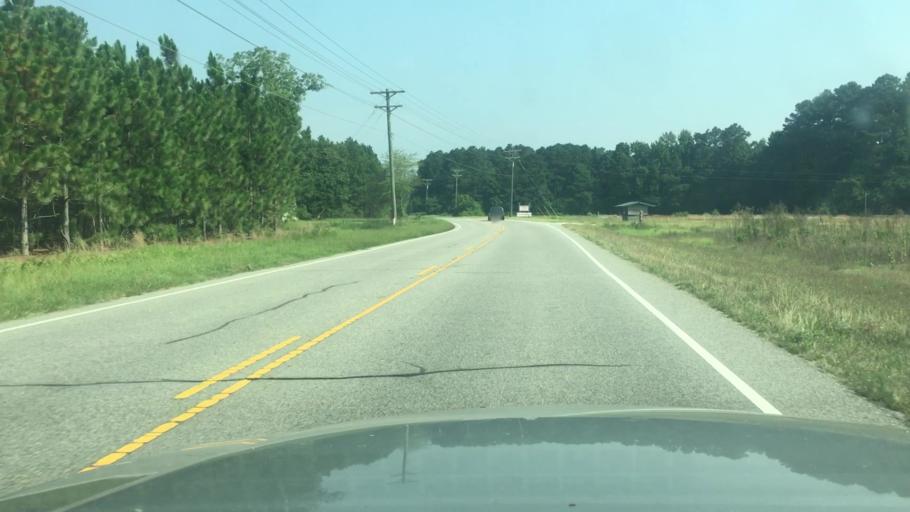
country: US
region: North Carolina
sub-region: Cumberland County
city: Hope Mills
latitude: 34.9112
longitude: -78.9051
